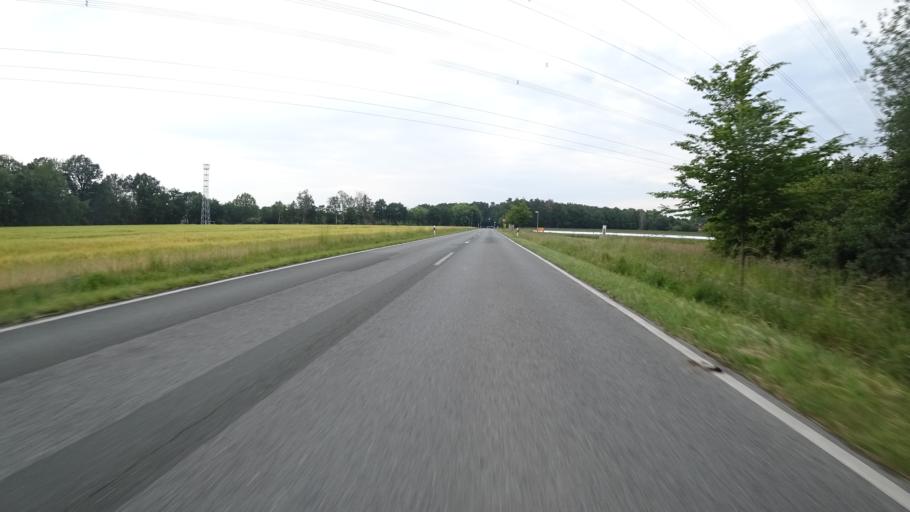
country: DE
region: North Rhine-Westphalia
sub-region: Regierungsbezirk Detmold
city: Guetersloh
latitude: 51.9316
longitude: 8.3773
